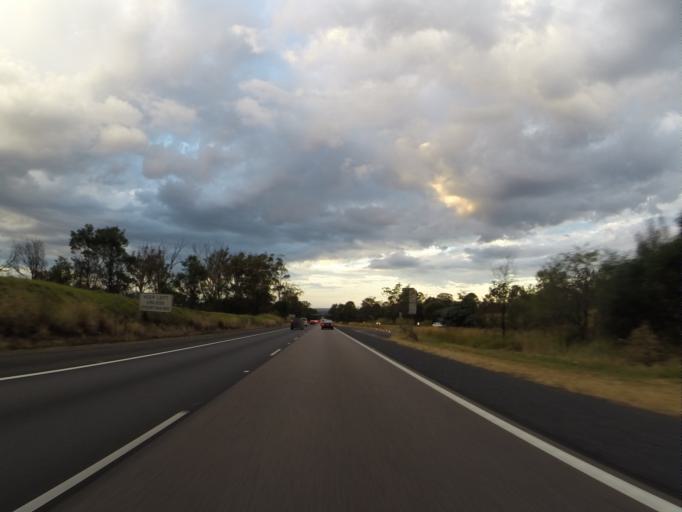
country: AU
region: New South Wales
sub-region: Wollondilly
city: Douglas Park
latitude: -34.2175
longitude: 150.6807
